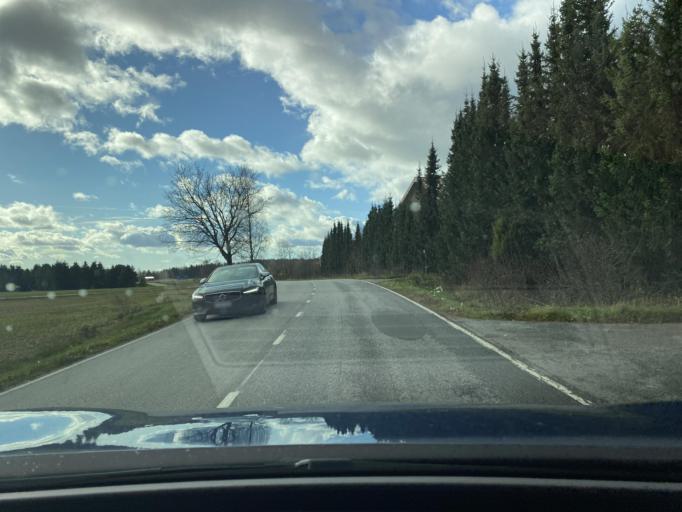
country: FI
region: Varsinais-Suomi
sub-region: Loimaa
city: Aura
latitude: 60.7051
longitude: 22.5934
